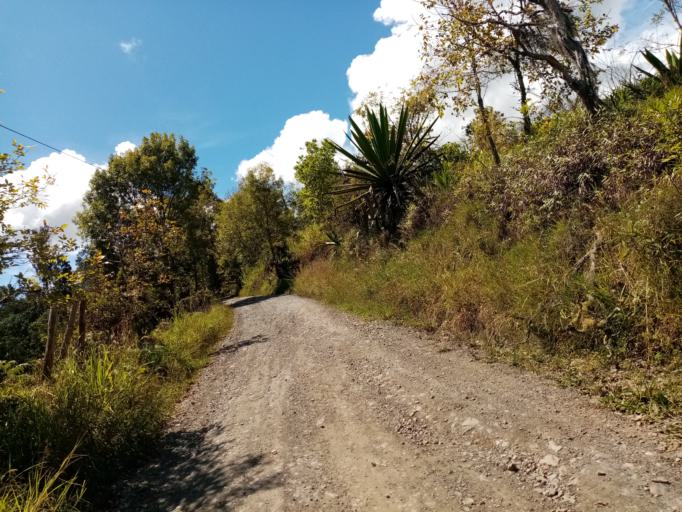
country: CO
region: Cundinamarca
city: Tenza
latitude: 5.0735
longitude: -73.4271
